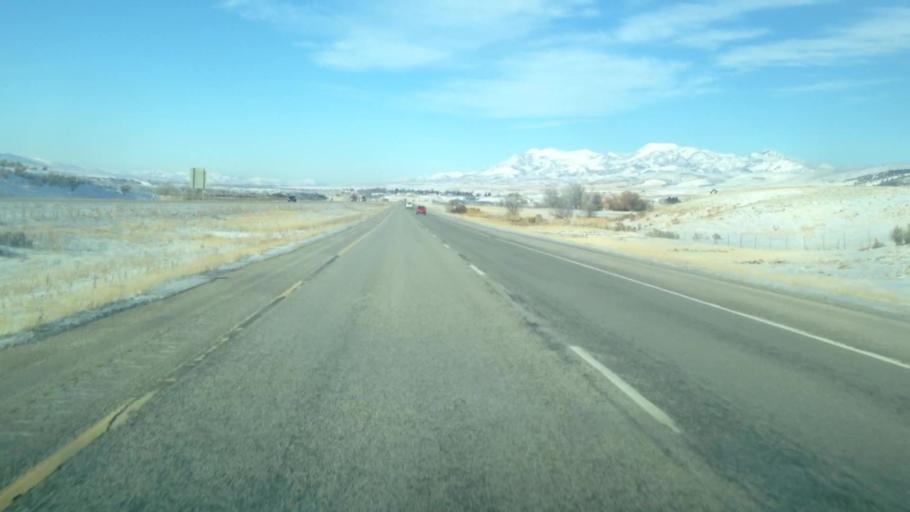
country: US
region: Idaho
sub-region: Oneida County
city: Malad City
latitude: 42.5191
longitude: -112.1700
